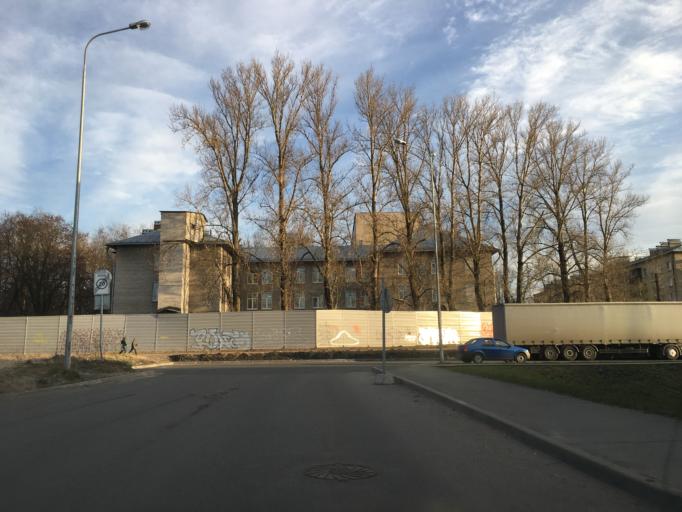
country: RU
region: St.-Petersburg
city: Uritsk
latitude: 59.8428
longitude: 30.1816
